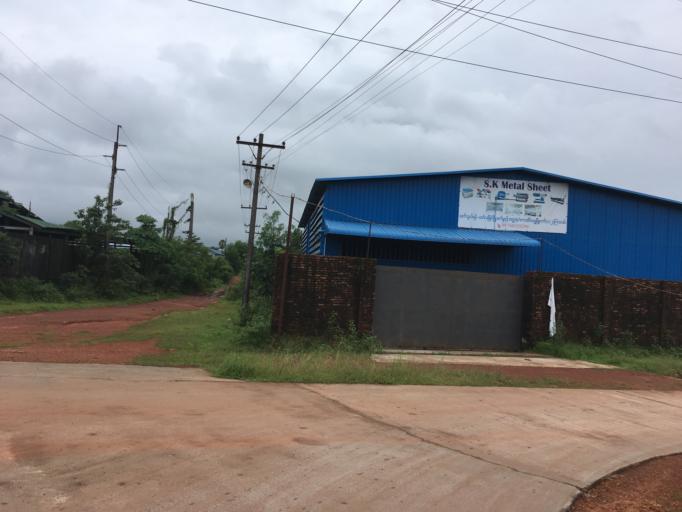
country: MM
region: Mon
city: Mawlamyine
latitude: 16.4788
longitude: 97.6751
